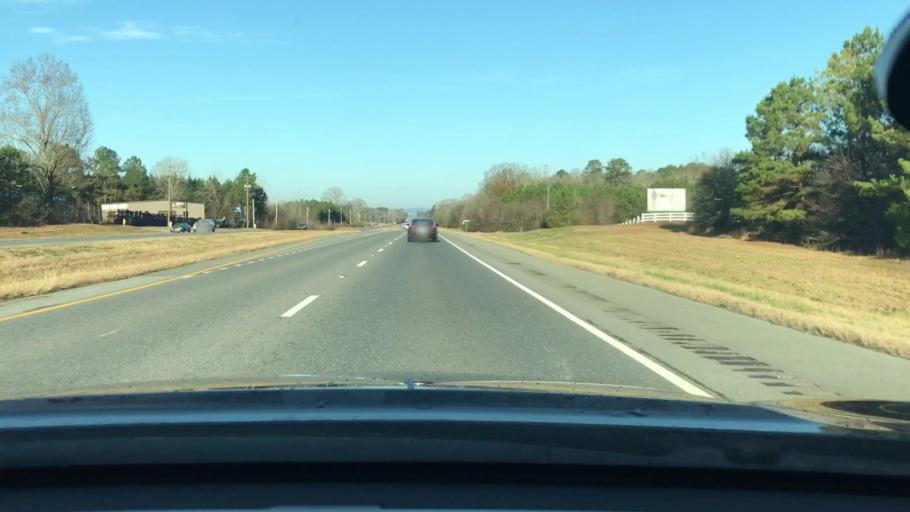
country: US
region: Alabama
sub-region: Shelby County
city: Harpersville
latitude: 33.3198
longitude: -86.3984
